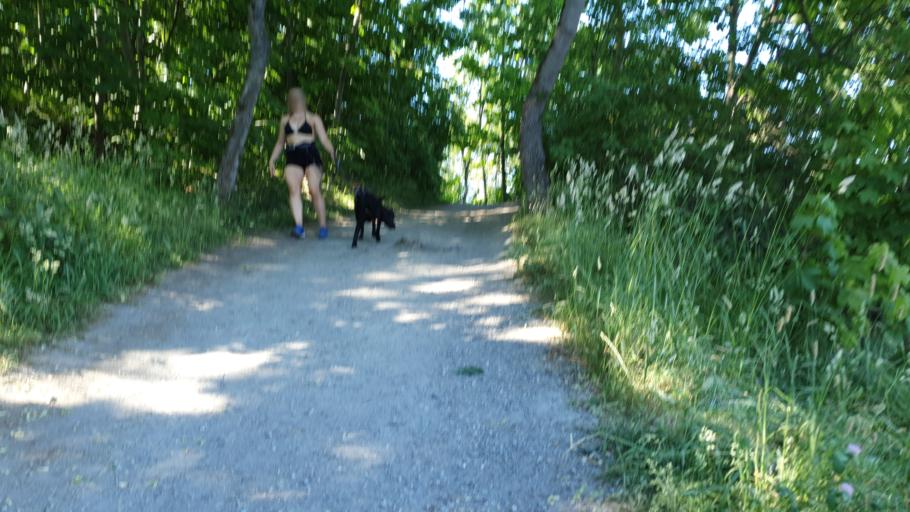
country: NO
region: Sor-Trondelag
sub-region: Trondheim
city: Trondheim
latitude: 63.4537
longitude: 10.4618
